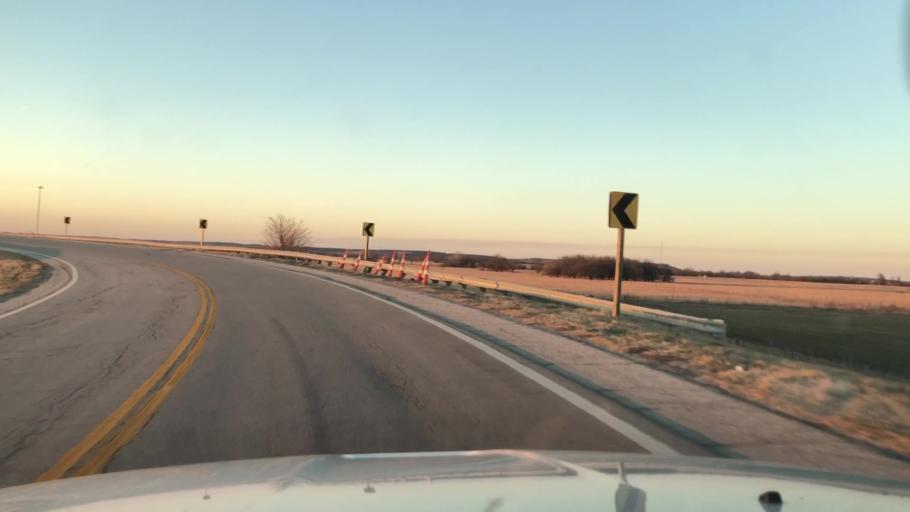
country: US
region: Kansas
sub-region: Montgomery County
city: Caney
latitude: 37.0660
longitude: -95.9249
